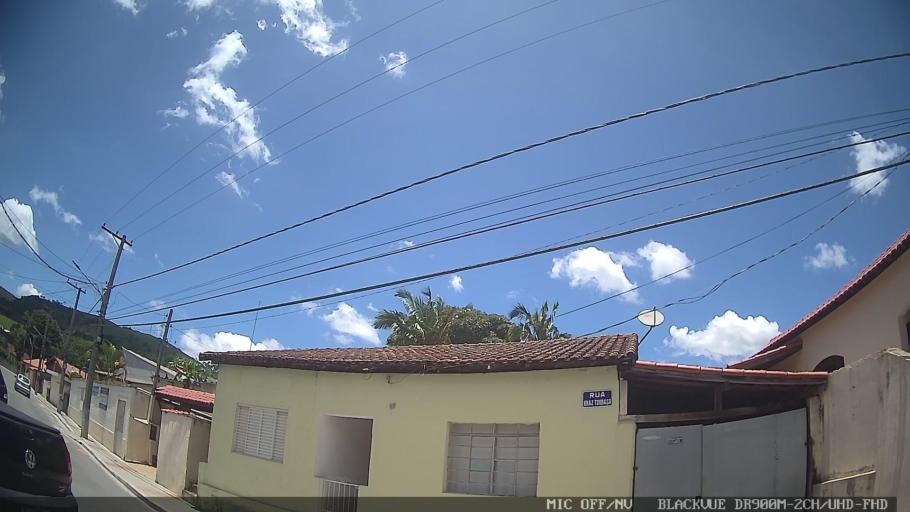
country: BR
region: Sao Paulo
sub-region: Santa Branca
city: Santa Branca
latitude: -23.5294
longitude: -45.8436
